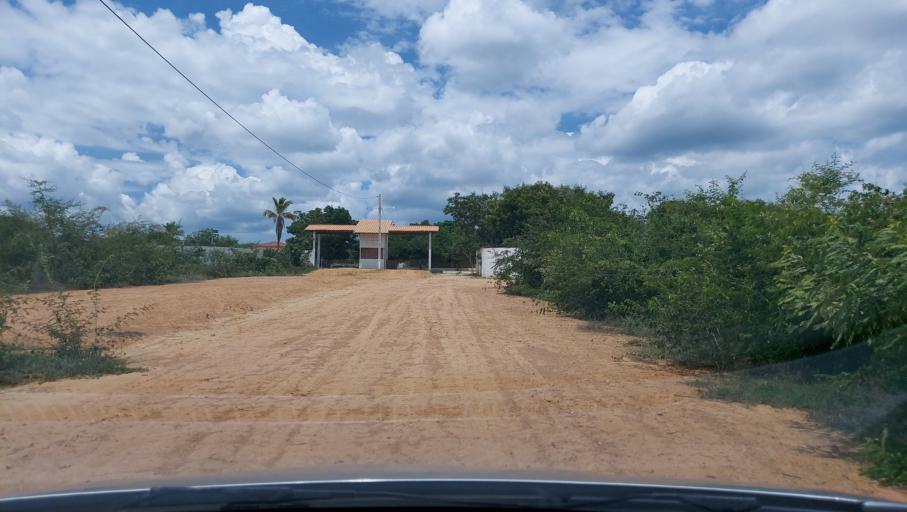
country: BR
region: Bahia
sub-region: Oliveira Dos Brejinhos
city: Beira Rio
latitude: -12.0134
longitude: -42.6307
